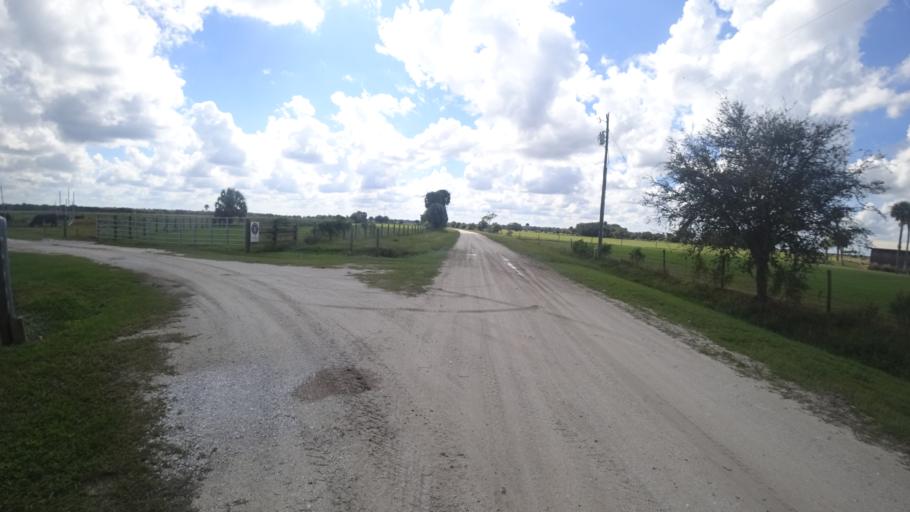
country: US
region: Florida
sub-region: Sarasota County
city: Warm Mineral Springs
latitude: 27.2535
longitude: -82.1625
